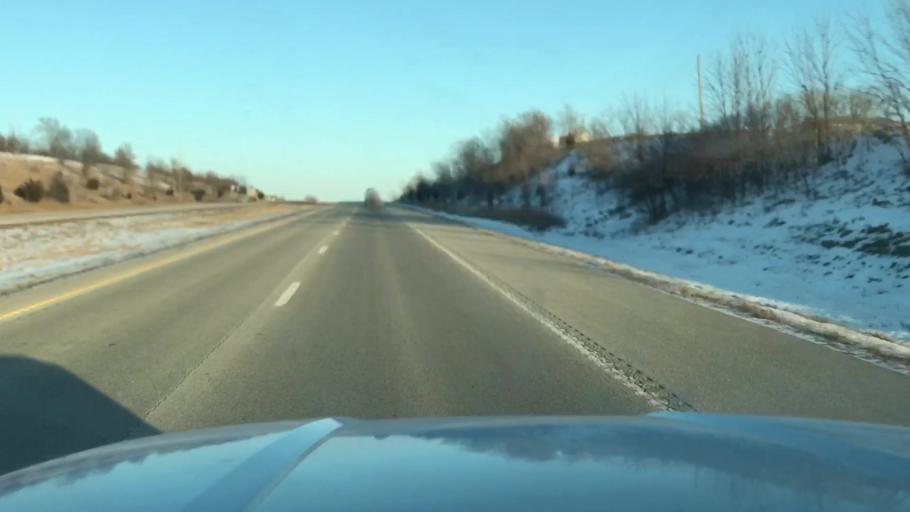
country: US
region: Missouri
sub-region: Buchanan County
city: Saint Joseph
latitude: 39.7476
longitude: -94.7104
